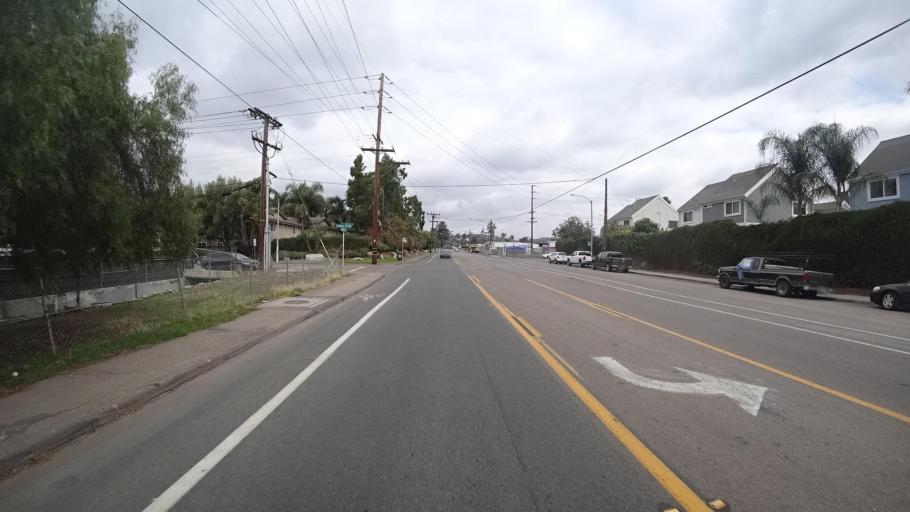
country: US
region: California
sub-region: San Diego County
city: Spring Valley
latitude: 32.7385
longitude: -117.0057
